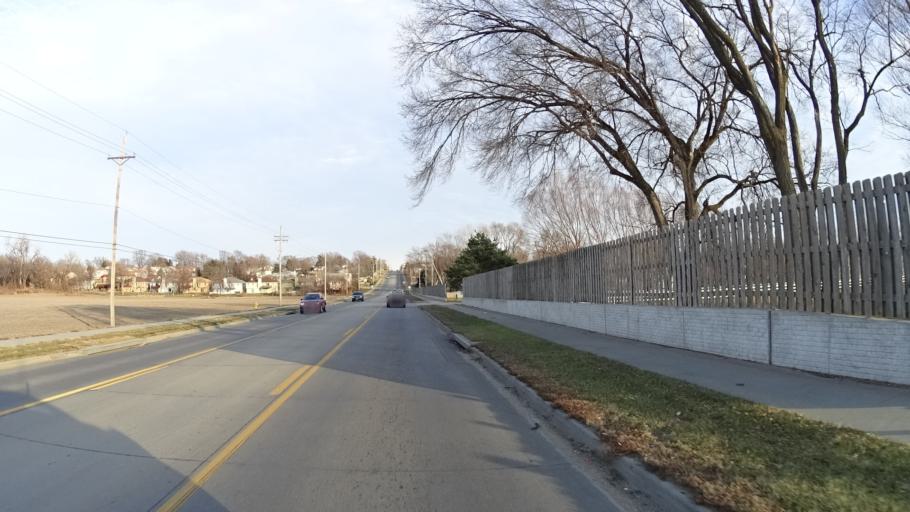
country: US
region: Nebraska
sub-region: Sarpy County
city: La Vista
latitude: 41.1907
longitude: -96.0029
